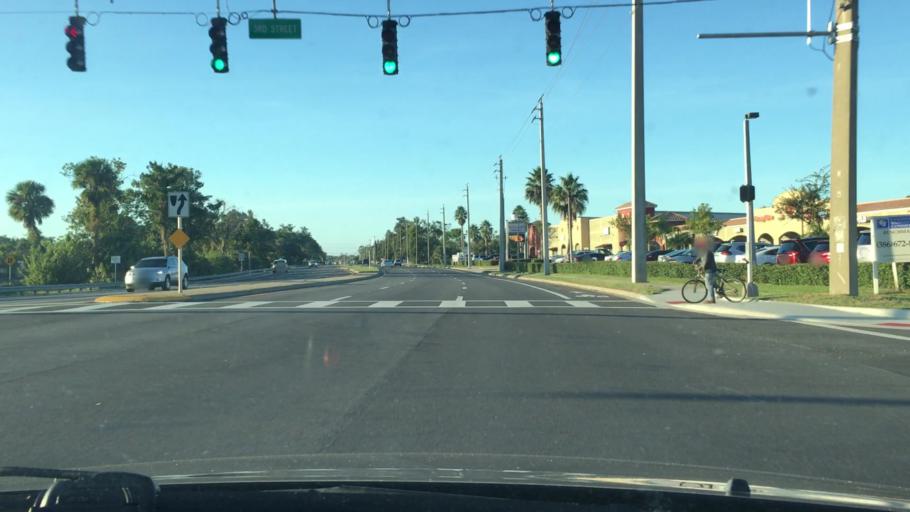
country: US
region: Florida
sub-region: Volusia County
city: Holly Hill
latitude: 29.2248
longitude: -81.0496
